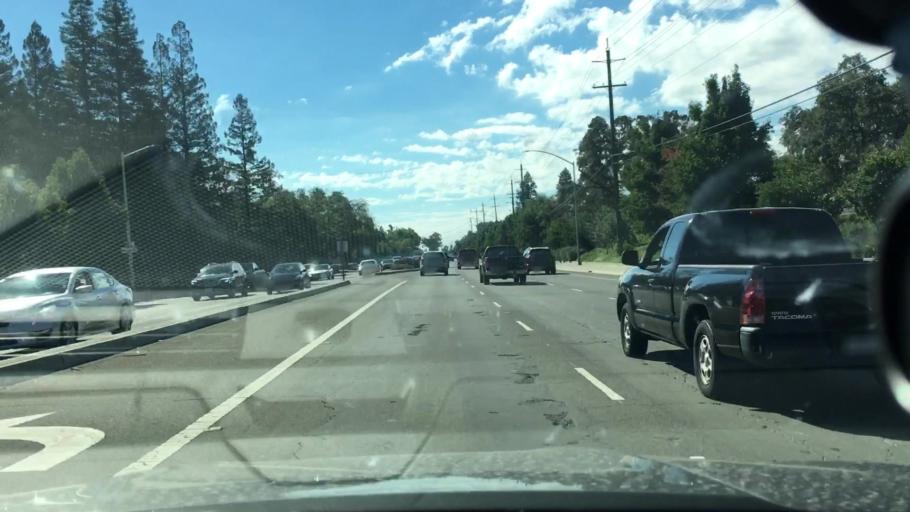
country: US
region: California
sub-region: Sacramento County
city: Arden-Arcade
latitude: 38.6231
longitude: -121.3830
